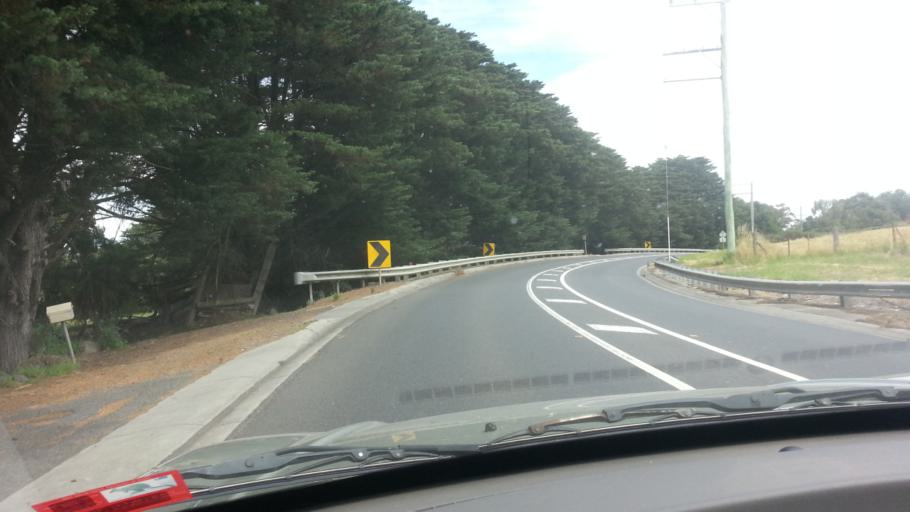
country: AU
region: Victoria
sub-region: Yarra Ranges
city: Lysterfield
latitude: -37.9170
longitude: 145.3004
